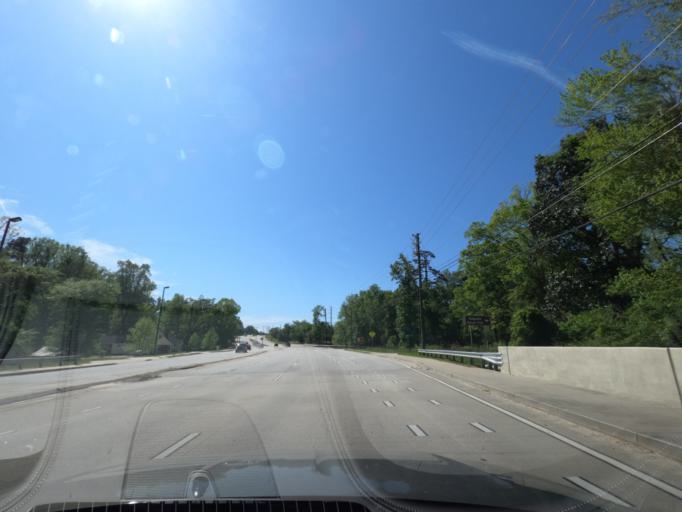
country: US
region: Georgia
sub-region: Columbia County
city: Martinez
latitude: 33.4706
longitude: -82.1051
